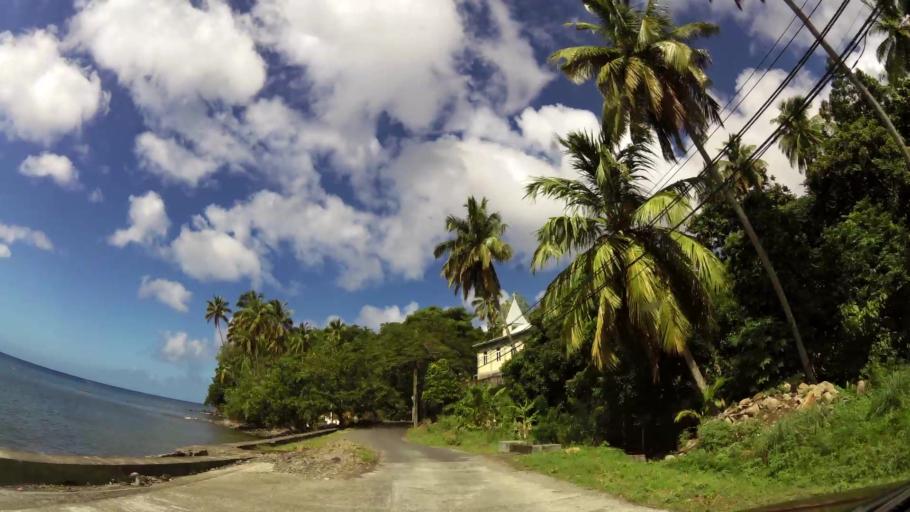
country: DM
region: Saint John
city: Portsmouth
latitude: 15.6117
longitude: -61.4647
